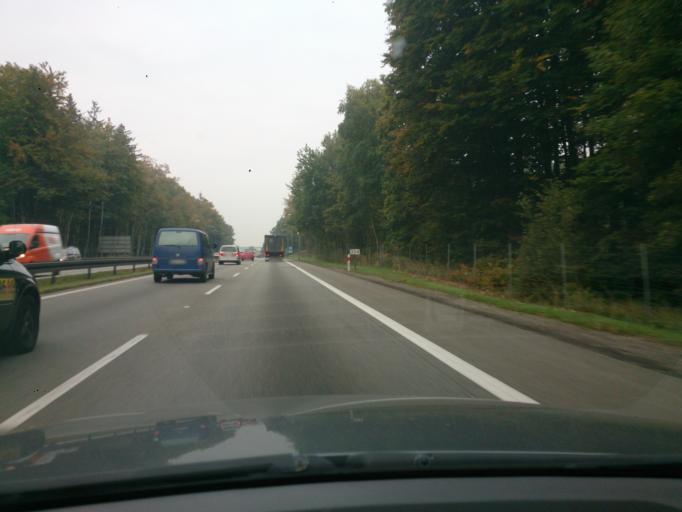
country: PL
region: Pomeranian Voivodeship
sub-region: Gdynia
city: Wielki Kack
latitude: 54.4413
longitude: 18.4893
